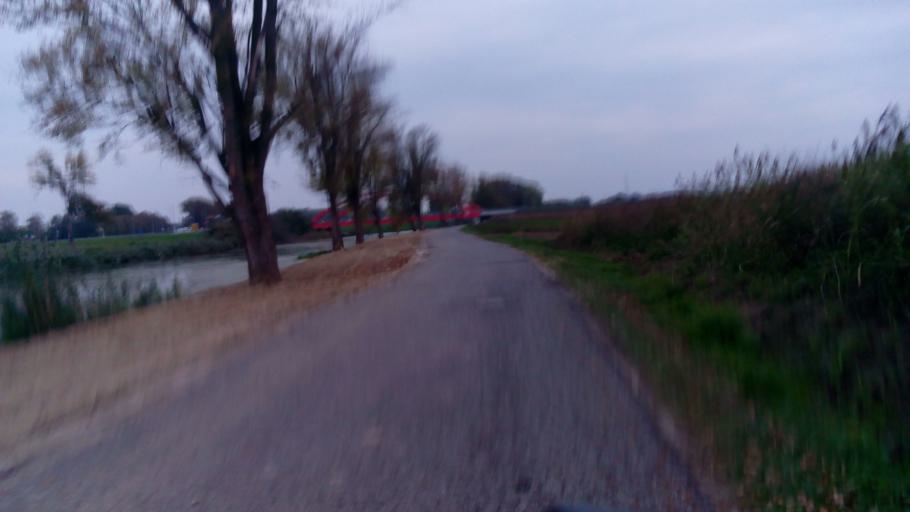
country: HR
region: Vukovarsko-Srijemska
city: Vinkovci
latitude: 45.2642
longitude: 18.8114
